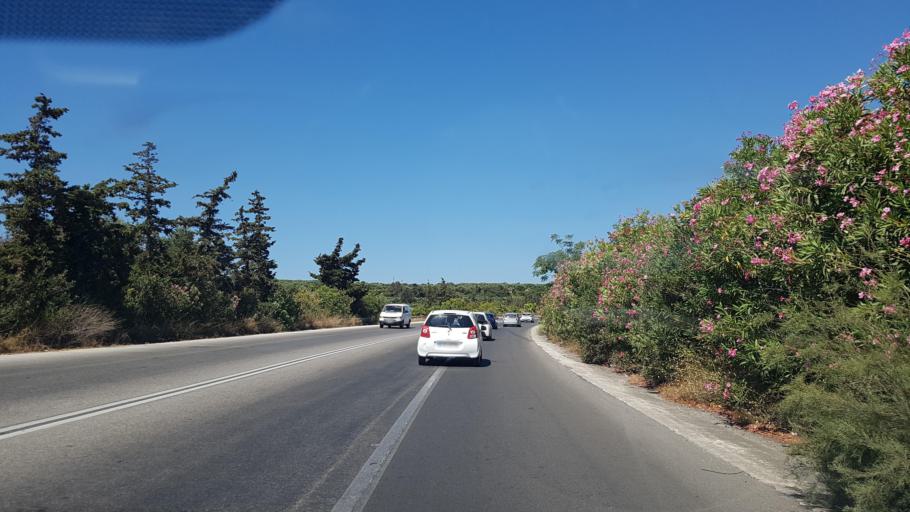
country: GR
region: Crete
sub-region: Nomos Chanias
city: Gerani
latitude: 35.5135
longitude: 23.8552
